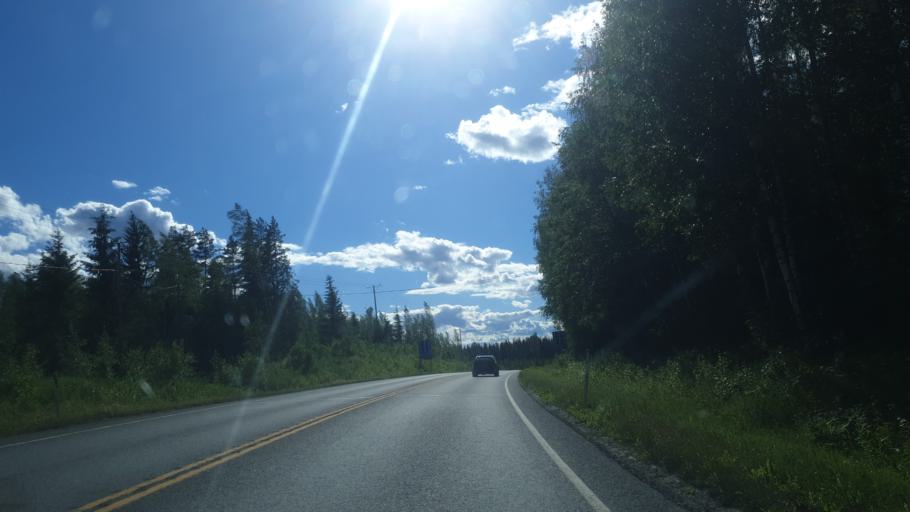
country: FI
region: Southern Savonia
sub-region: Mikkeli
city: Mikkeli
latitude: 61.7088
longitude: 27.4444
